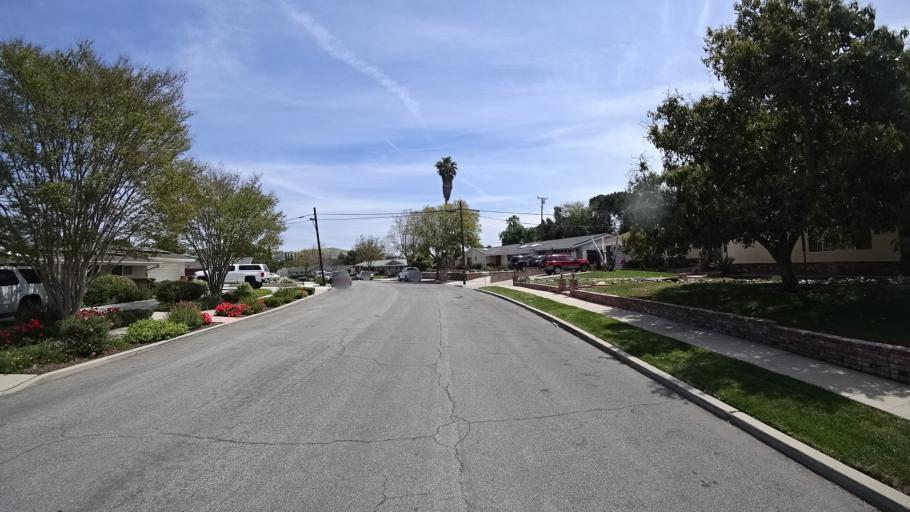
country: US
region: California
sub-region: Ventura County
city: Thousand Oaks
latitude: 34.1915
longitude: -118.8703
